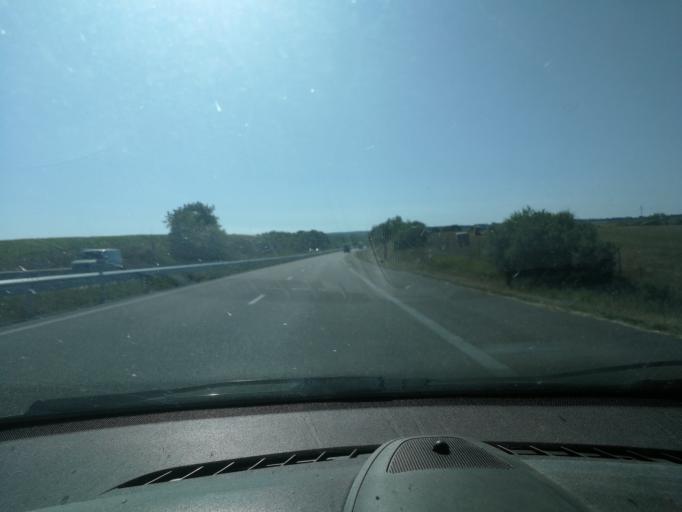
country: FR
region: Lorraine
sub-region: Departement de la Moselle
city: Phalsbourg
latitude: 48.7945
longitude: 7.2082
